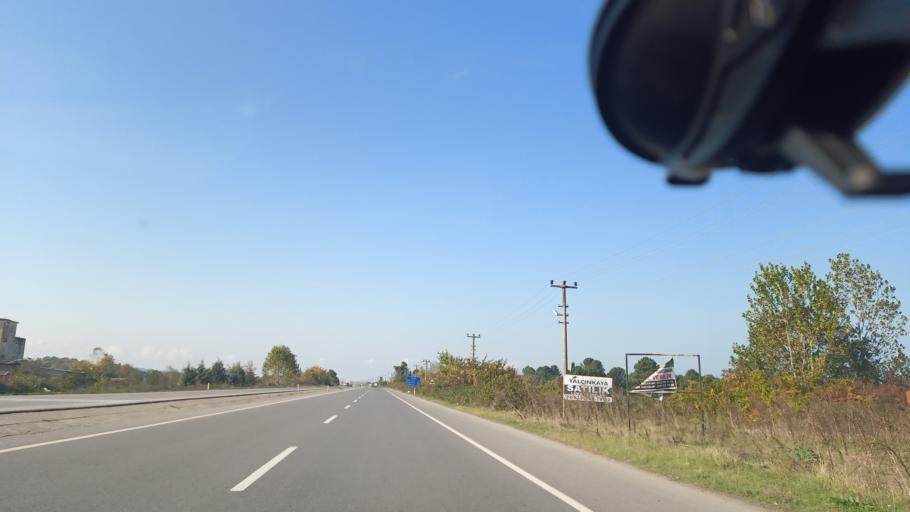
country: TR
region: Sakarya
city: Karasu
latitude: 41.0766
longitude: 30.7795
